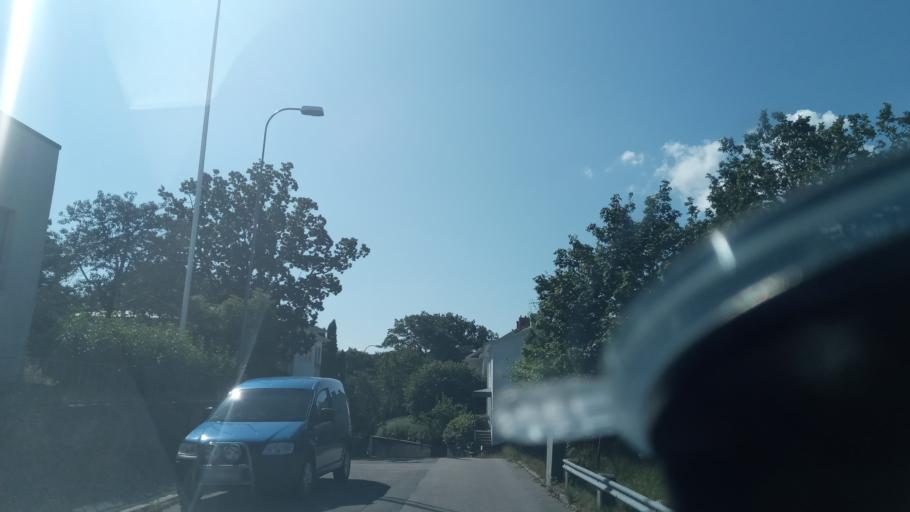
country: SE
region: Vaestra Goetaland
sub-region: Molndal
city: Moelndal
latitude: 57.6927
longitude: 12.0112
